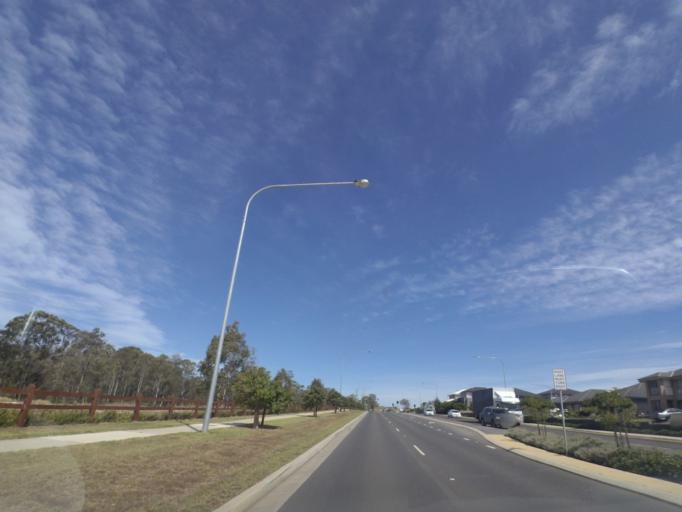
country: AU
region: New South Wales
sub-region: Camden
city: Narellan Vale
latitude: -34.0266
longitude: 150.7848
